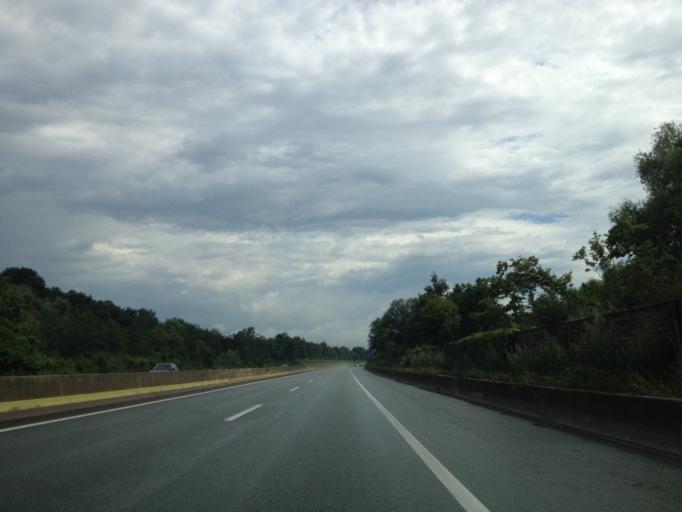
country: AT
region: Styria
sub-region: Politischer Bezirk Hartberg-Fuerstenfeld
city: Sebersdorf
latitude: 47.1934
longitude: 15.9938
